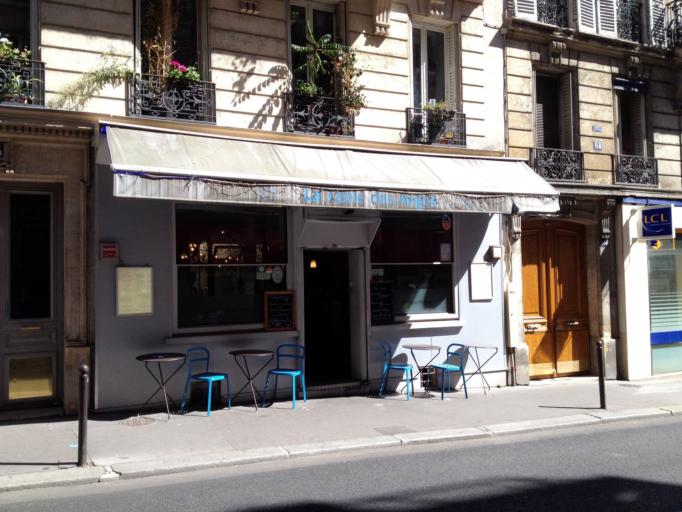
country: FR
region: Ile-de-France
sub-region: Paris
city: Saint-Ouen
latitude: 48.8810
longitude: 2.3403
